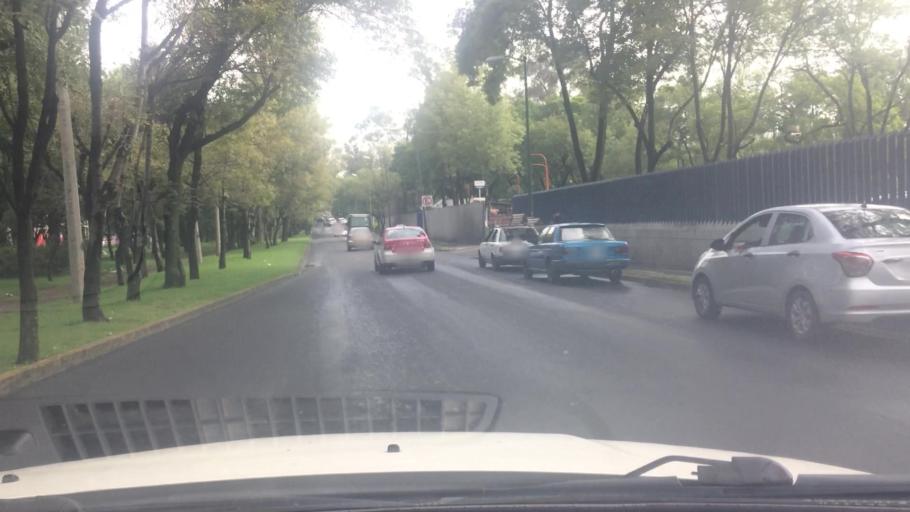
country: MX
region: Mexico City
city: Colonia Nativitas
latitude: 19.3502
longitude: -99.1301
